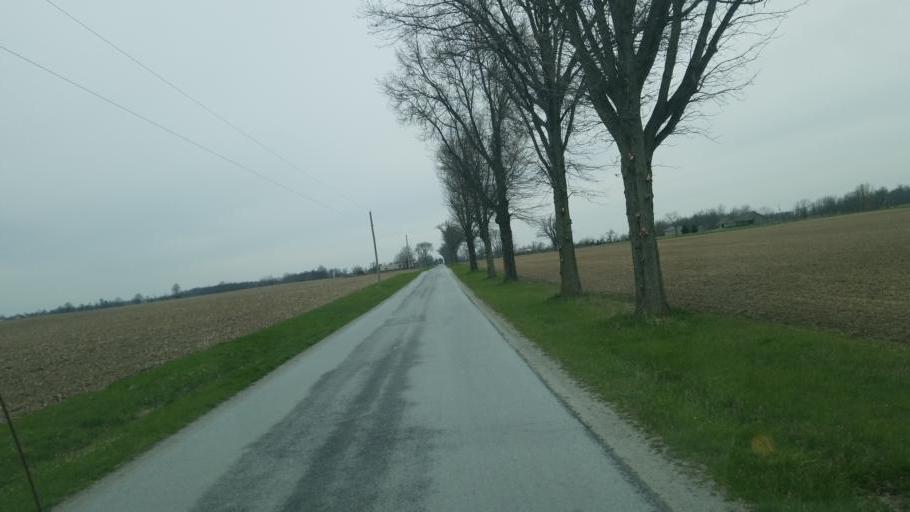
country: US
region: Ohio
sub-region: Hardin County
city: Forest
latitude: 40.8177
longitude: -83.4730
